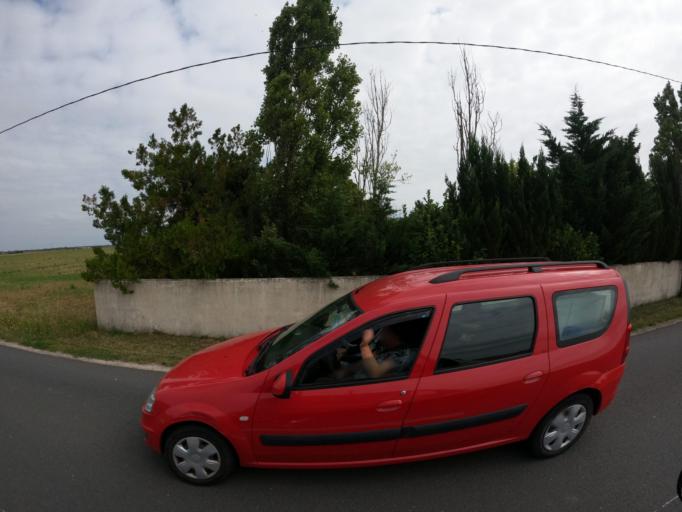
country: FR
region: Poitou-Charentes
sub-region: Departement de la Charente-Maritime
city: Marans
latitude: 46.2887
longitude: -0.9494
